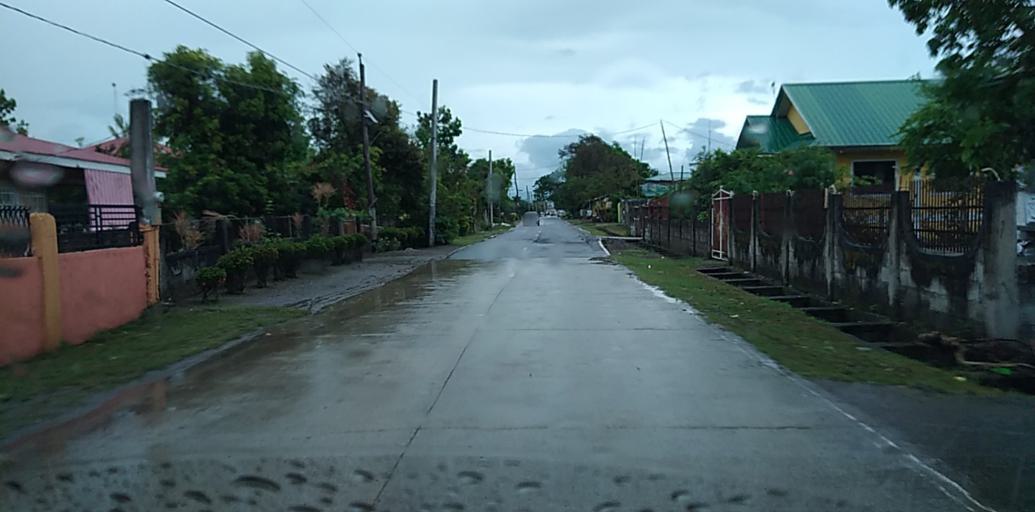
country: PH
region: Central Luzon
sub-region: Province of Pampanga
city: Salapungan
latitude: 15.1354
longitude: 120.9165
